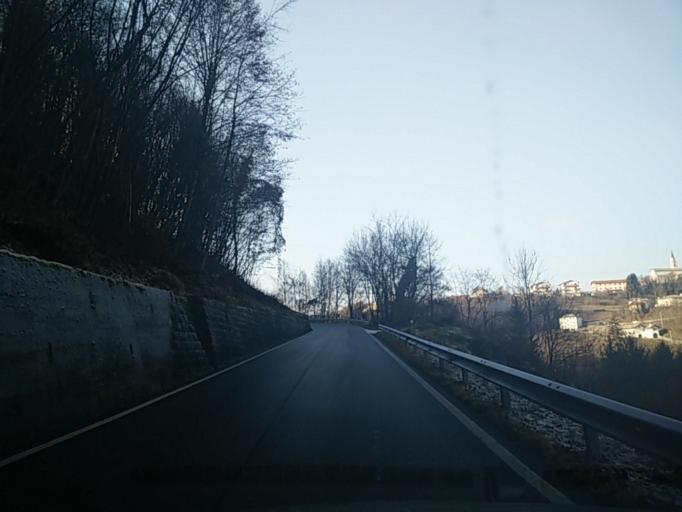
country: IT
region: Veneto
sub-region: Provincia di Belluno
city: Trichiana
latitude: 46.0352
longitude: 12.1672
